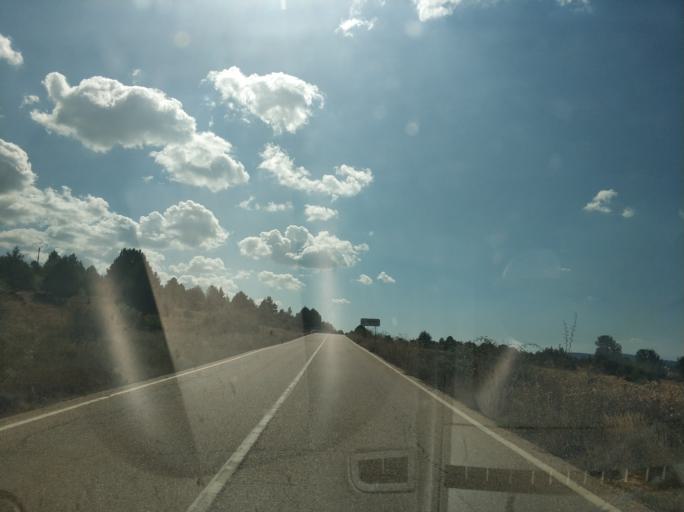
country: ES
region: Castille and Leon
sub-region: Provincia de Soria
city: Casarejos
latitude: 41.7778
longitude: -3.0266
